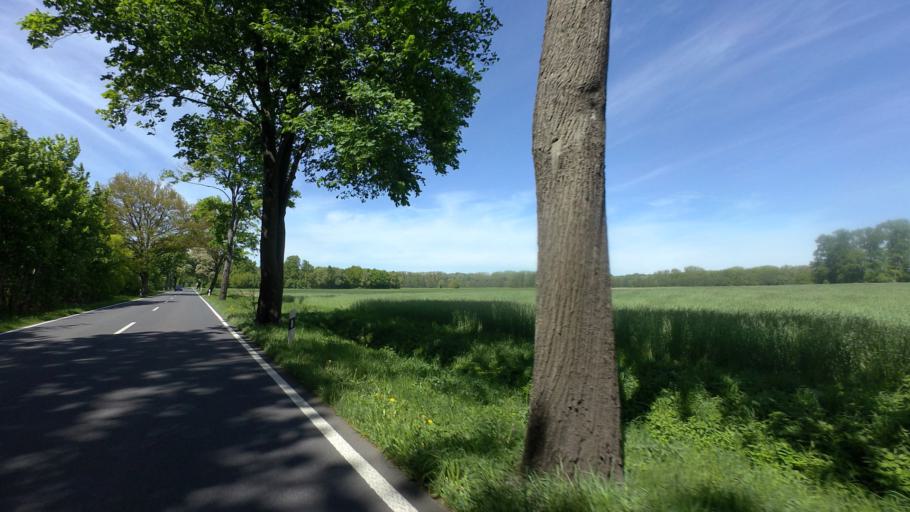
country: DE
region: Brandenburg
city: Baruth
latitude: 52.0783
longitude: 13.4543
